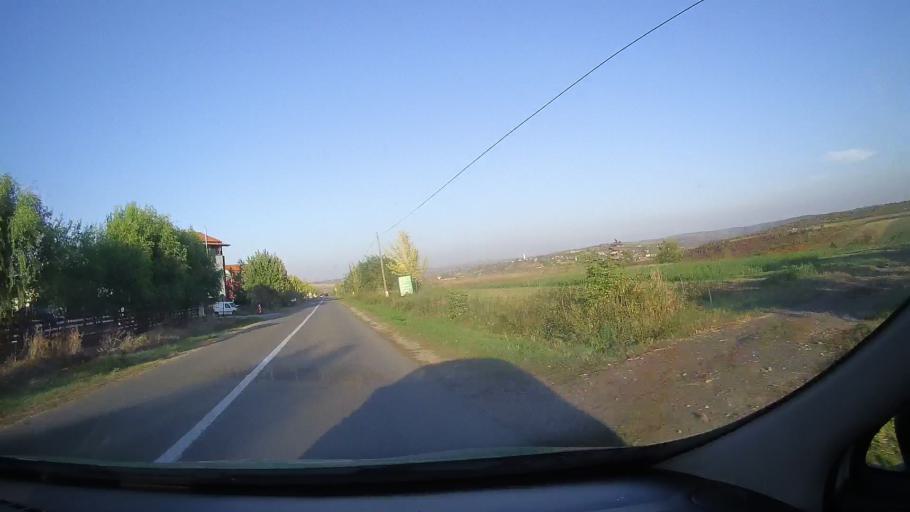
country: RO
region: Bihor
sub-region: Comuna Paleu
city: Paleu
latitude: 47.1109
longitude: 21.9358
